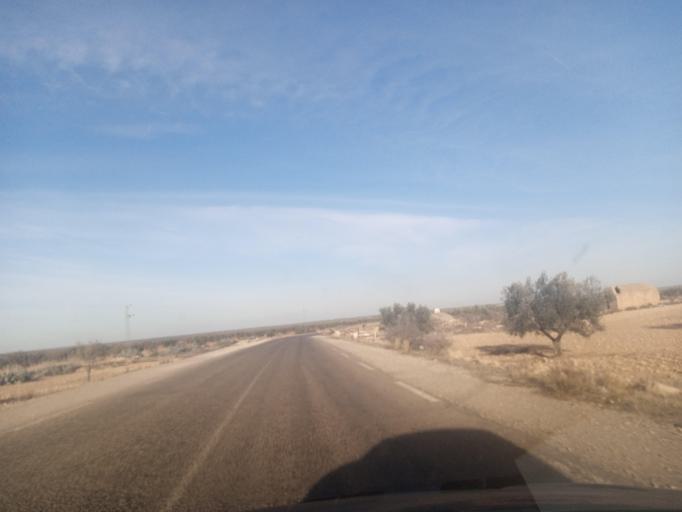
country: TN
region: Safaqis
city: Bi'r `Ali Bin Khalifah
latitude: 34.9293
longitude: 10.3235
